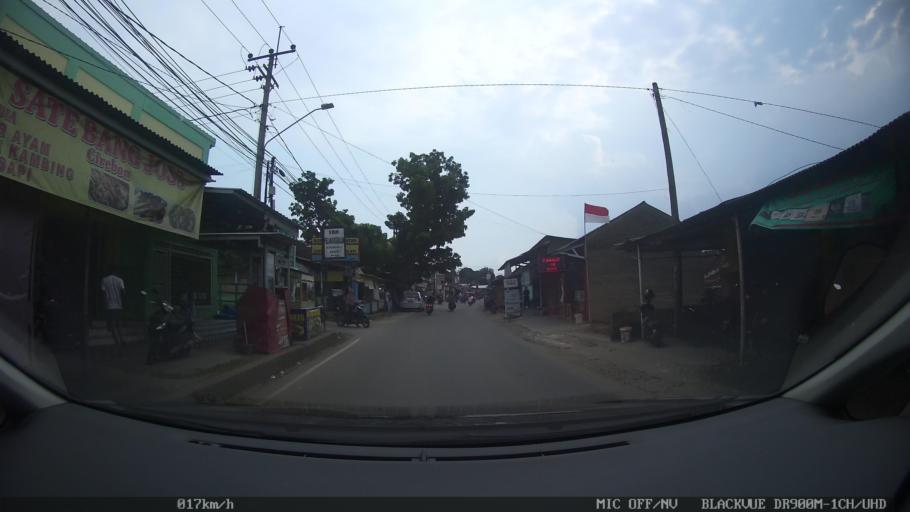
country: ID
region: Lampung
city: Kedaton
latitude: -5.3528
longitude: 105.2386
